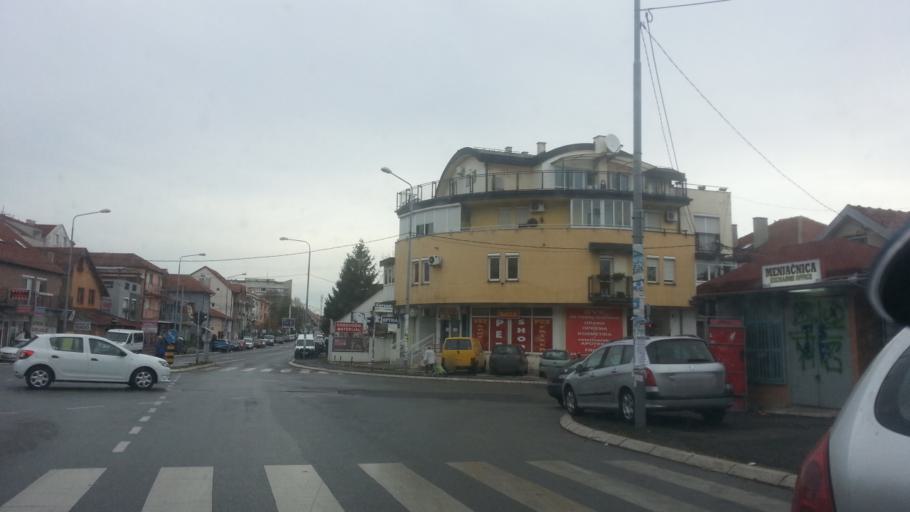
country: RS
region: Central Serbia
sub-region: Belgrade
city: Zemun
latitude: 44.8424
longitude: 20.3936
